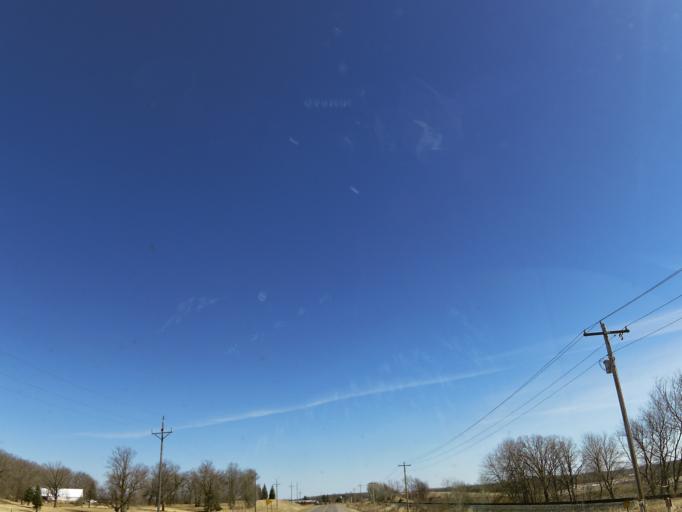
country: US
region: Minnesota
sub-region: Wright County
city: Annandale
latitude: 45.2428
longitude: -94.0666
